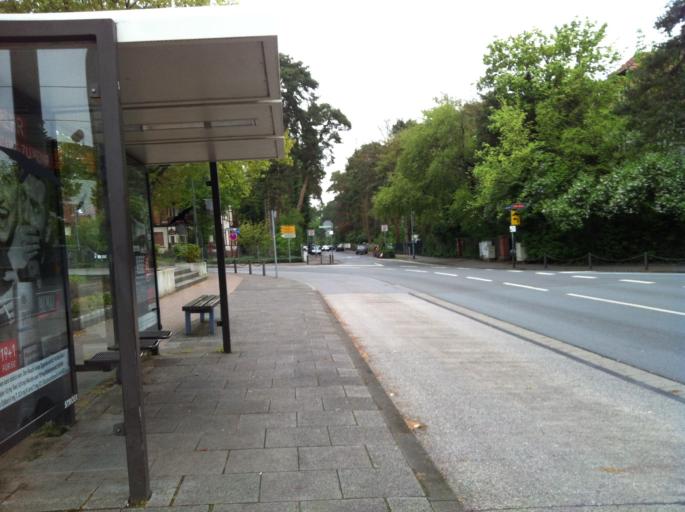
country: DE
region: Rheinland-Pfalz
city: Budenheim
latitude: 50.0016
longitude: 8.2042
